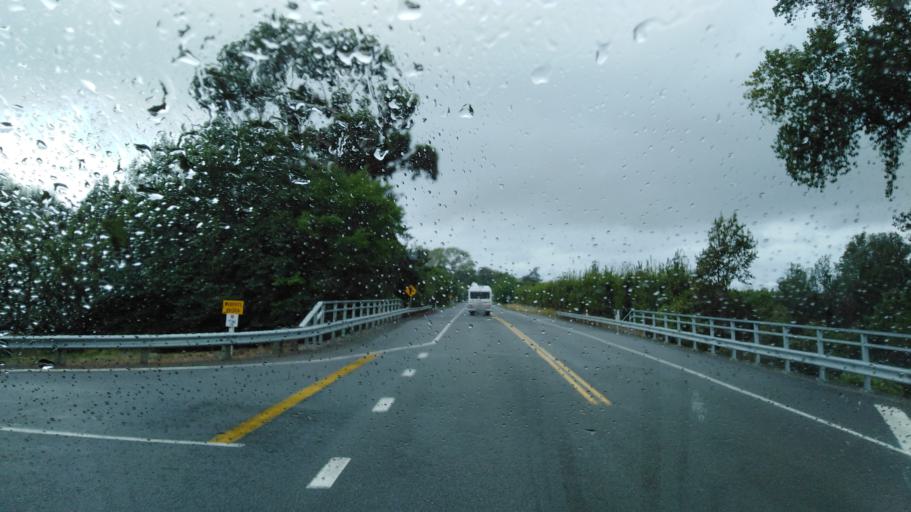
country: NZ
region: Marlborough
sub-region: Marlborough District
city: Blenheim
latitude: -41.4587
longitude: 173.9481
